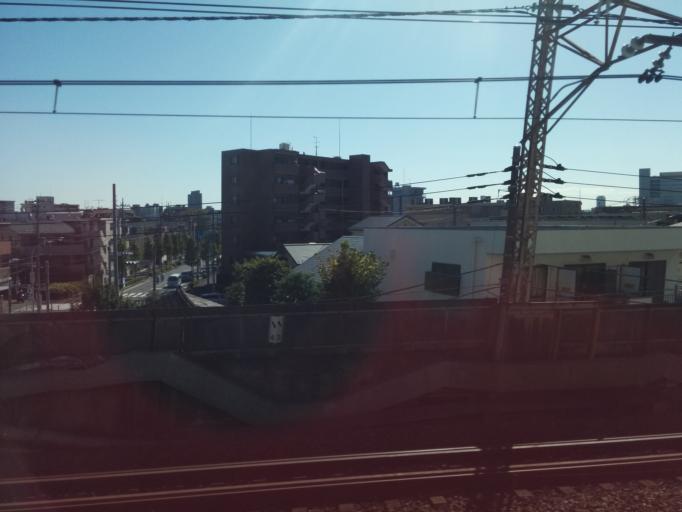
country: JP
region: Kanagawa
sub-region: Kawasaki-shi
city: Kawasaki
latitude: 35.5784
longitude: 139.6645
